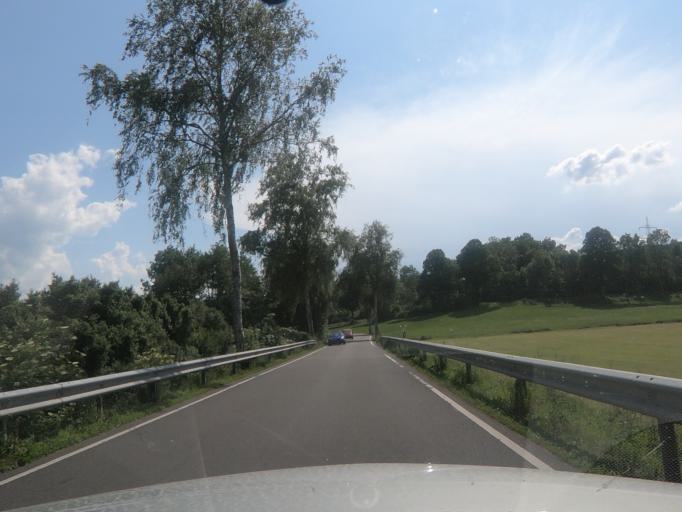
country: DE
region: North Rhine-Westphalia
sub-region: Regierungsbezirk Arnsberg
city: Finnentrop
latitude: 51.1115
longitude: 7.9615
